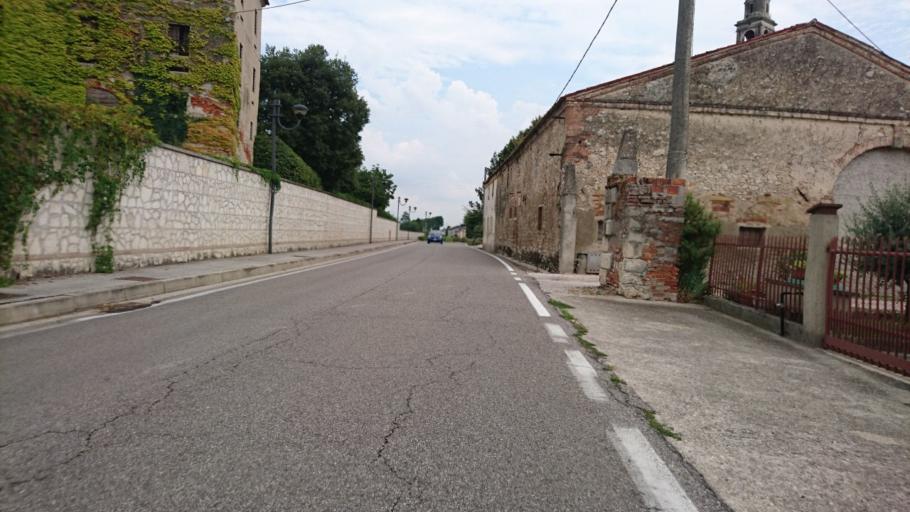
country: IT
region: Veneto
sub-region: Provincia di Vicenza
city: Montegalda
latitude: 45.4415
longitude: 11.6775
